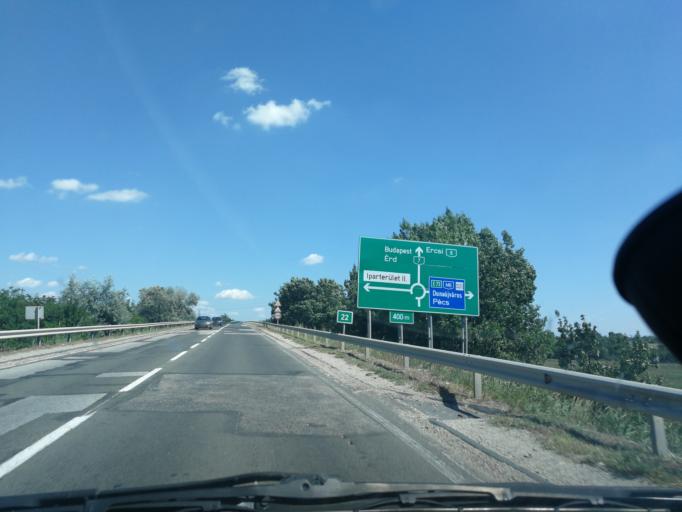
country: HU
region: Pest
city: Erd
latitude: 47.3613
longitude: 18.8979
